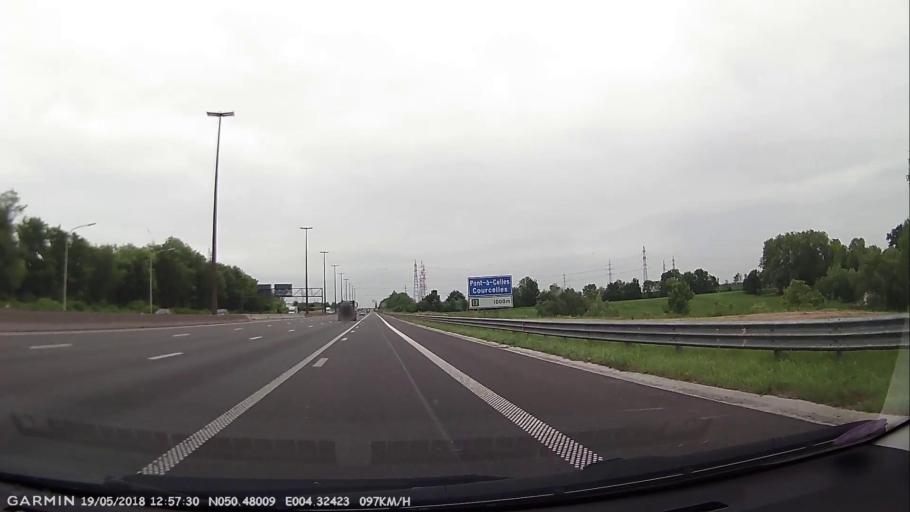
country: BE
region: Wallonia
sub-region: Province du Hainaut
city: Chapelle-lez-Herlaimont
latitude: 50.4801
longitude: 4.3244
